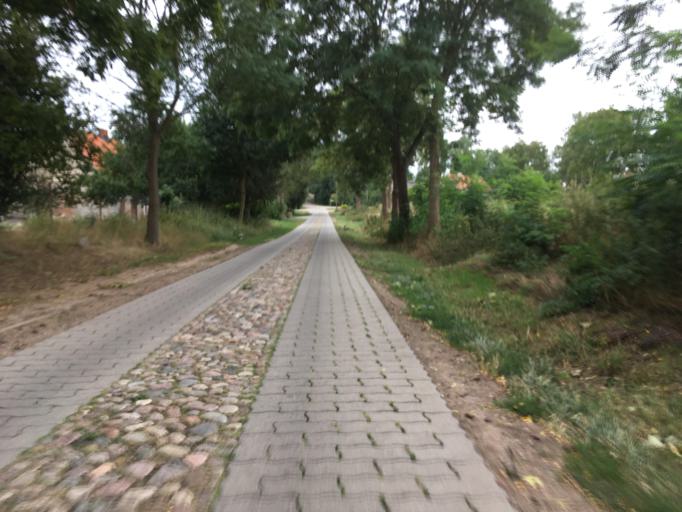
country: DE
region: Brandenburg
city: Pinnow
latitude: 53.0921
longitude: 14.1224
